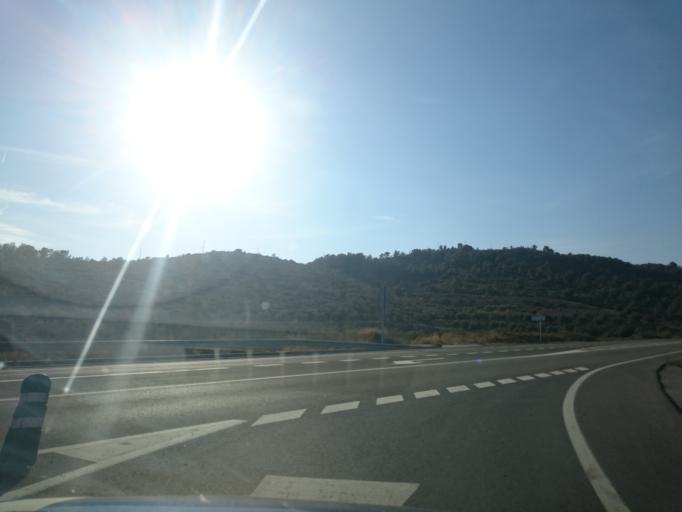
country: ES
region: Catalonia
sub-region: Provincia de Barcelona
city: Vilanova i la Geltru
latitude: 41.2550
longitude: 1.7171
